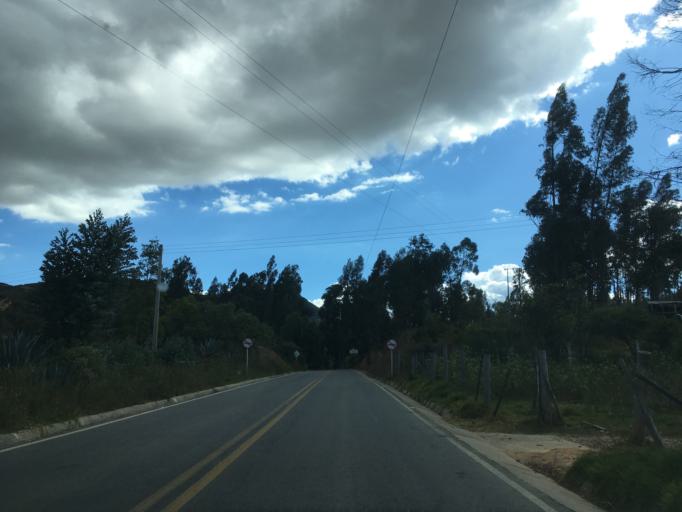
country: CO
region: Boyaca
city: Firavitoba
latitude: 5.6233
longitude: -73.0105
